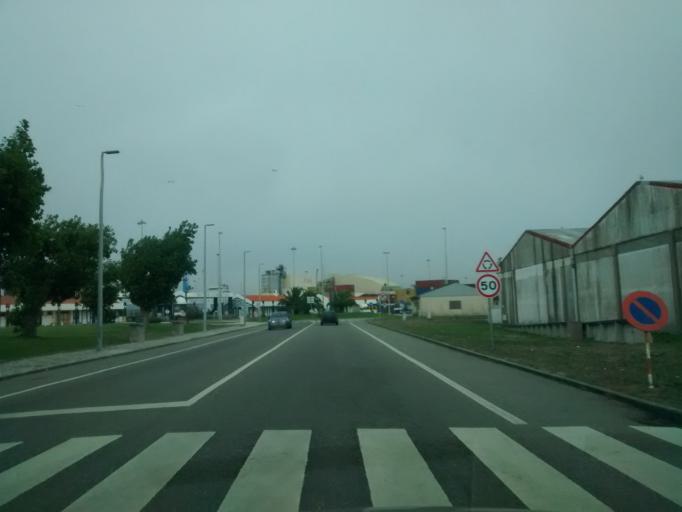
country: PT
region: Aveiro
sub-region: Ilhavo
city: Gafanha da Nazare
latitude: 40.6456
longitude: -8.7324
